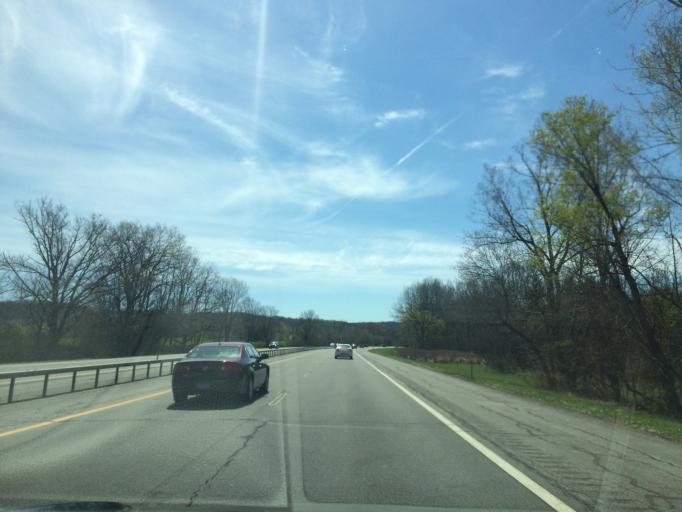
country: US
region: New York
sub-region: Monroe County
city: East Rochester
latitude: 43.0725
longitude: -77.4783
